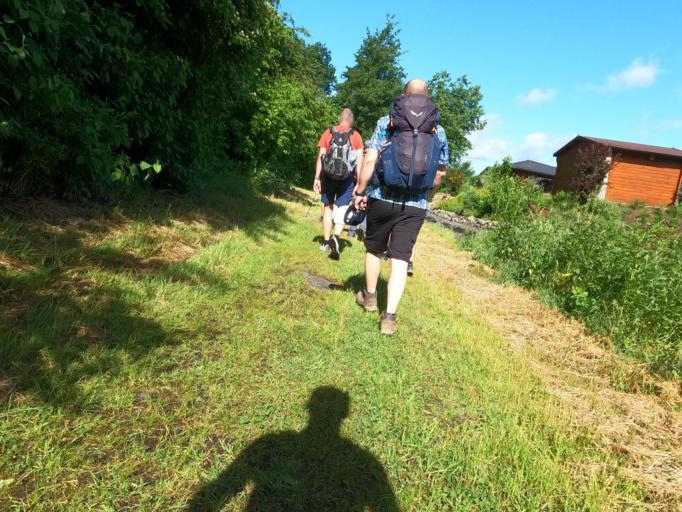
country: DE
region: Rheinland-Pfalz
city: Nister
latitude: 50.6736
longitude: 7.8355
